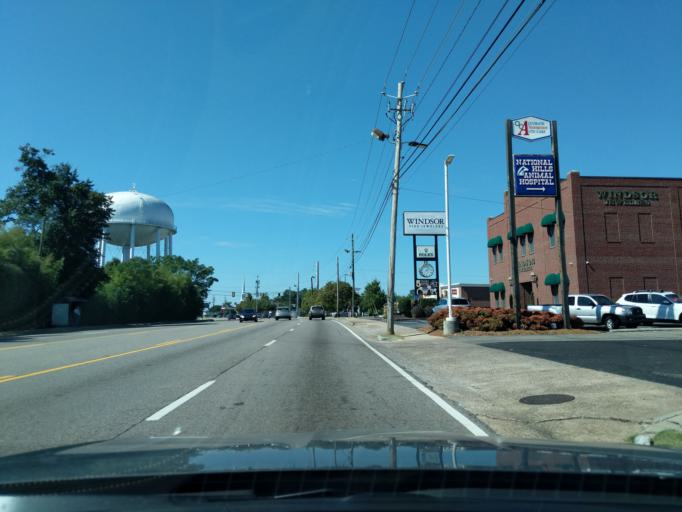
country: US
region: Georgia
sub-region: Columbia County
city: Martinez
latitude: 33.5078
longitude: -82.0212
